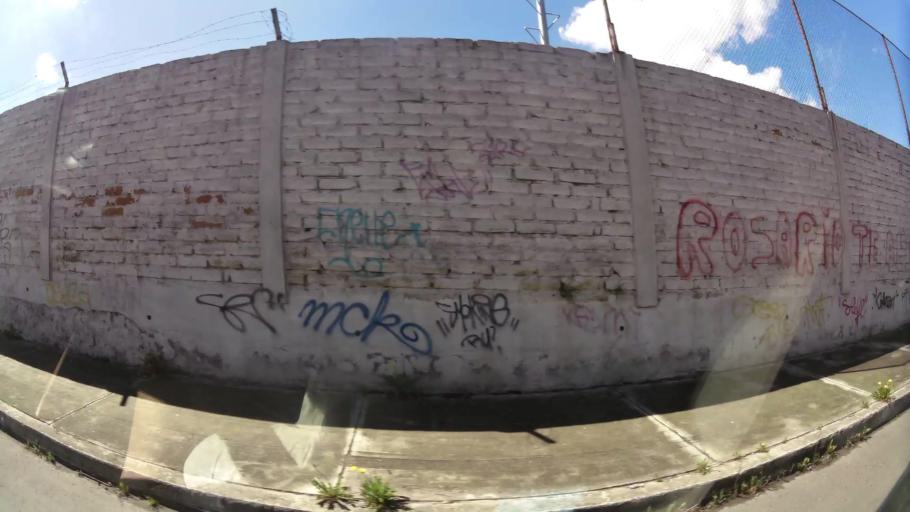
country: EC
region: Pichincha
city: Quito
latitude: -0.2963
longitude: -78.5436
